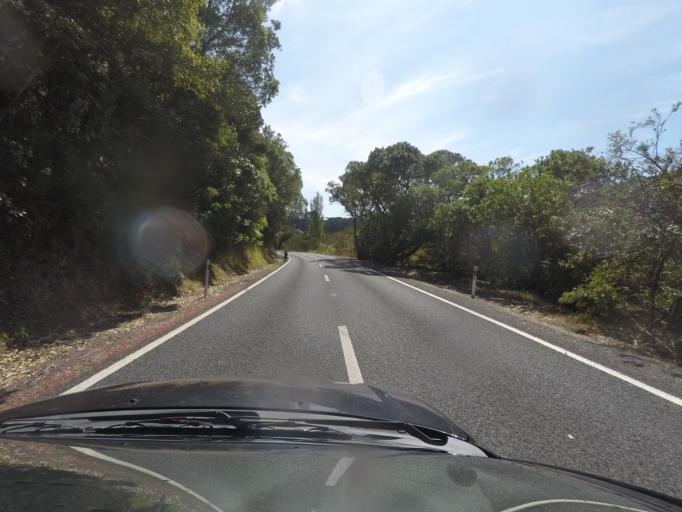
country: NZ
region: Auckland
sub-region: Auckland
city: Warkworth
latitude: -36.3068
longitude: 174.7819
